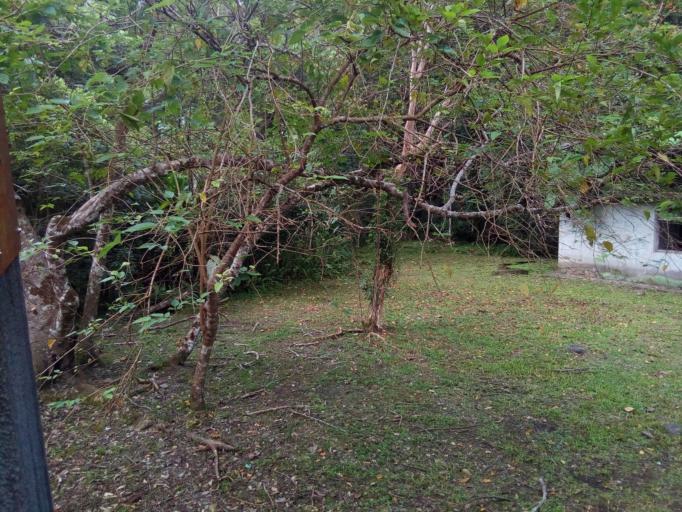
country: TW
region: Taiwan
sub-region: Taitung
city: Taitung
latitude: 23.3182
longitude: 121.2555
